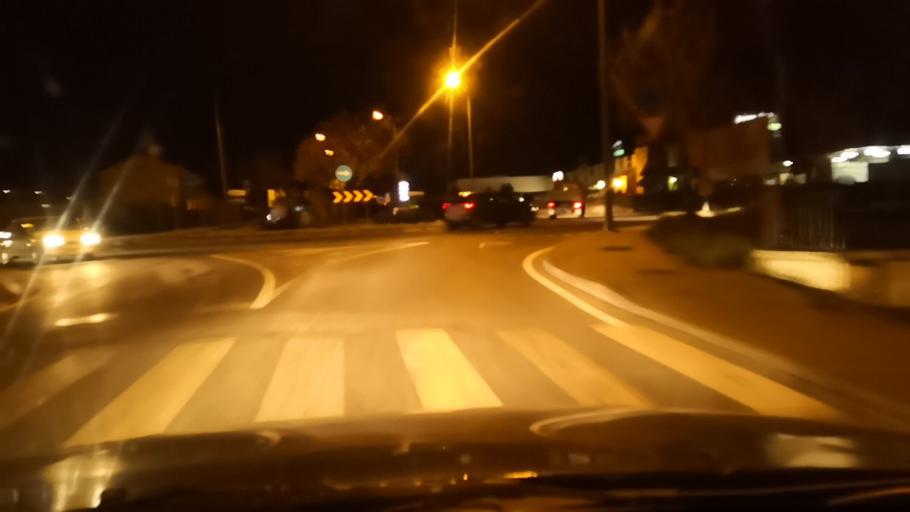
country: PT
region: Castelo Branco
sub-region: Concelho do Fundao
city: Fundao
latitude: 40.1635
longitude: -7.4974
